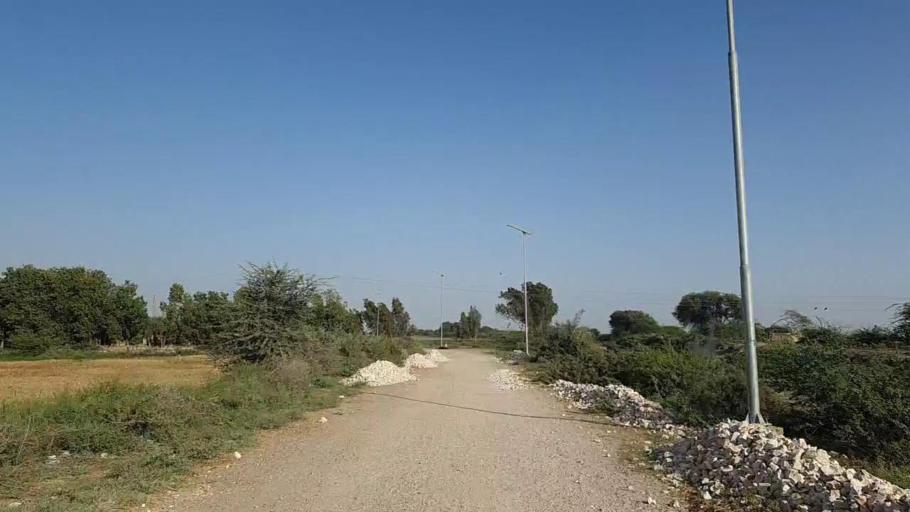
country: PK
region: Sindh
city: Jati
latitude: 24.4236
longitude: 68.2588
